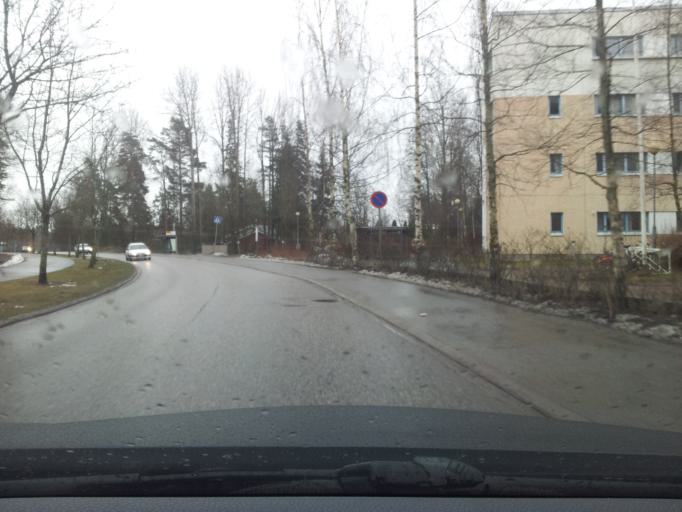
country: FI
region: Uusimaa
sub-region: Helsinki
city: Espoo
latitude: 60.1670
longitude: 24.6782
